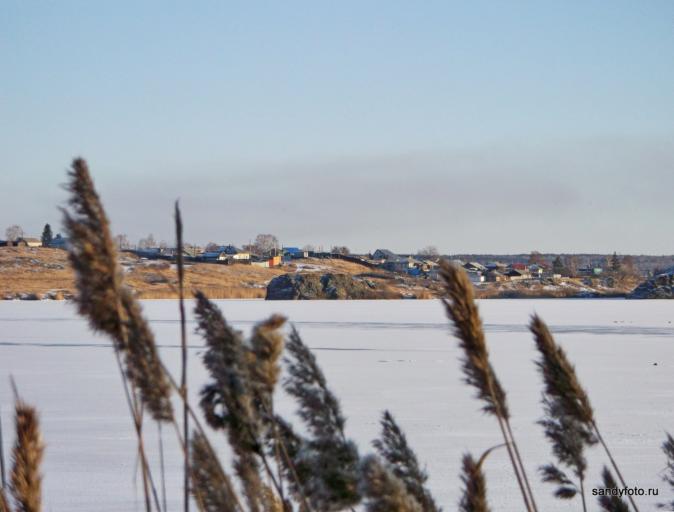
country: RU
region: Chelyabinsk
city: Troitsk
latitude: 54.0787
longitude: 61.5617
